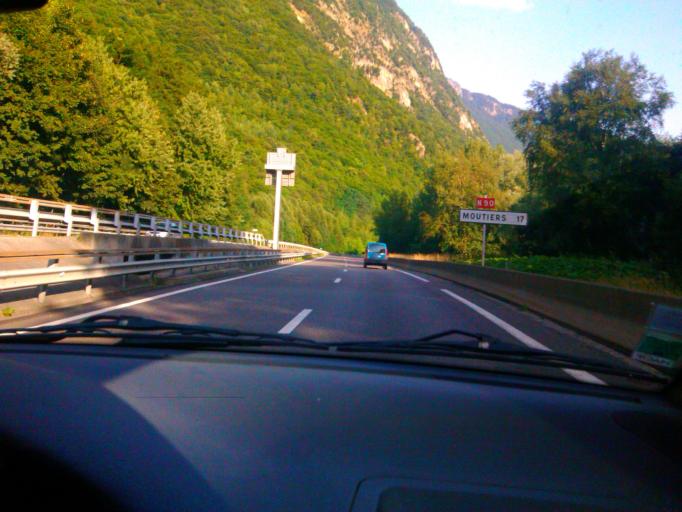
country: FR
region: Rhone-Alpes
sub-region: Departement de la Savoie
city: La Bathie
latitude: 45.5829
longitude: 6.4567
